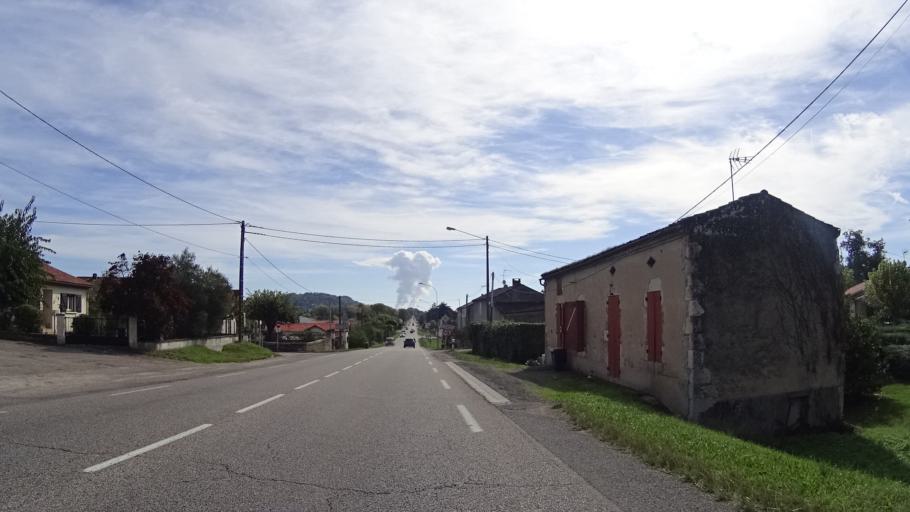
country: FR
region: Aquitaine
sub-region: Departement du Lot-et-Garonne
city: Castelculier
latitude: 44.1734
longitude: 0.6902
